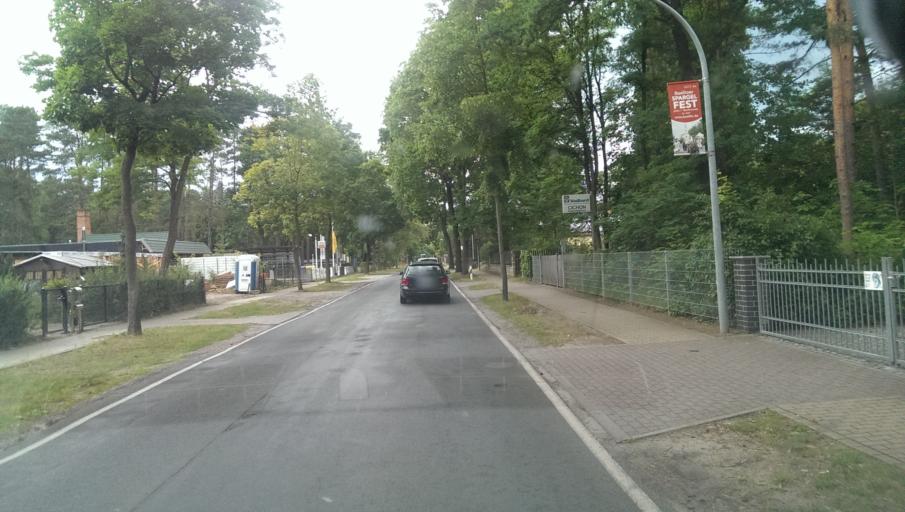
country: DE
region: Brandenburg
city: Fichtenwalde
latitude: 52.2781
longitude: 12.8918
